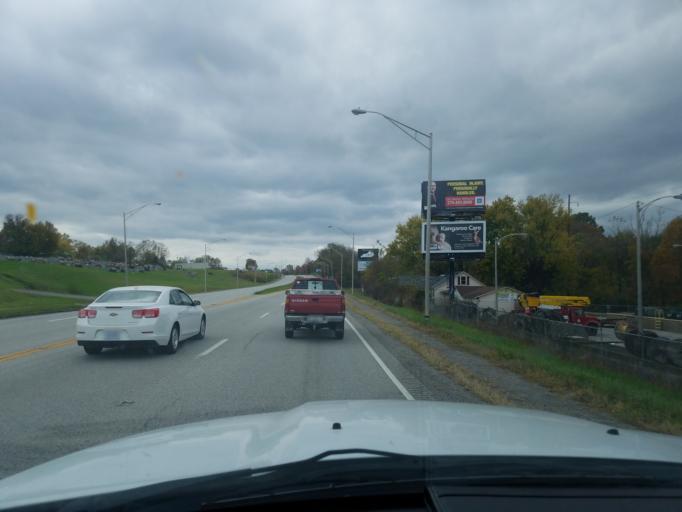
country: US
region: Kentucky
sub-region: Taylor County
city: Campbellsville
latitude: 37.3401
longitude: -85.3509
